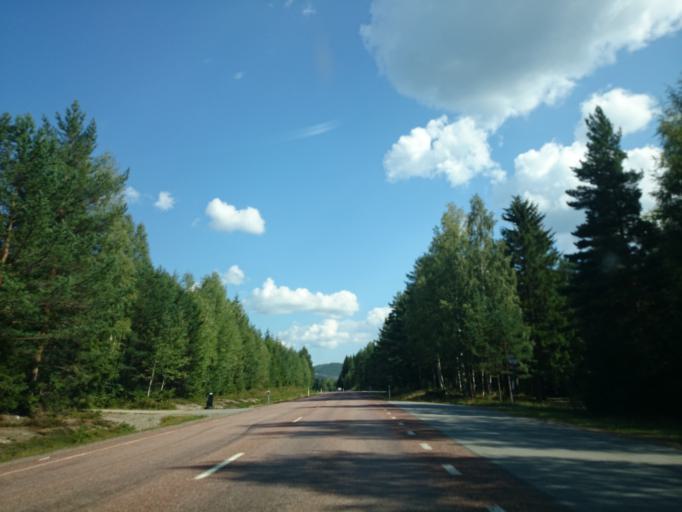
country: SE
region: Gaevleborg
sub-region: Ljusdals Kommun
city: Jaervsoe
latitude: 61.8054
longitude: 16.2545
